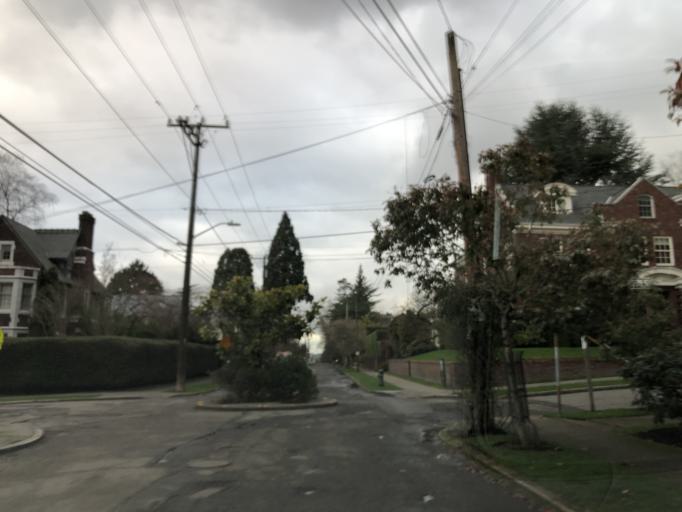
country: US
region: Washington
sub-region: King County
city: Seattle
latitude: 47.6321
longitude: -122.3191
